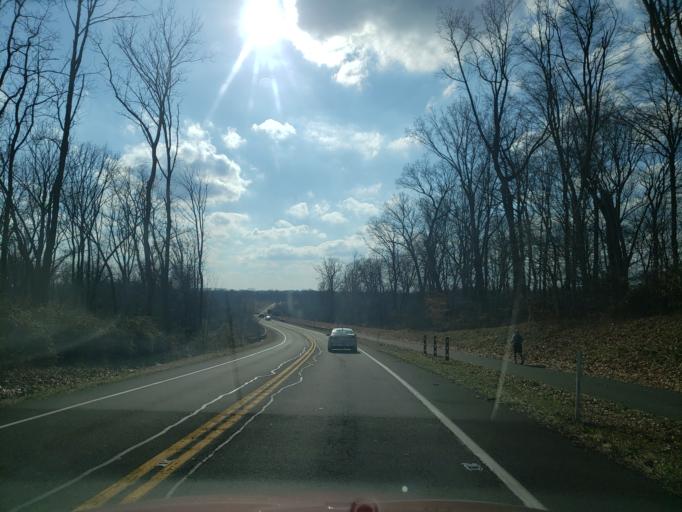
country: US
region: Pennsylvania
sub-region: Bucks County
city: New Britain
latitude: 40.2891
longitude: -75.1621
